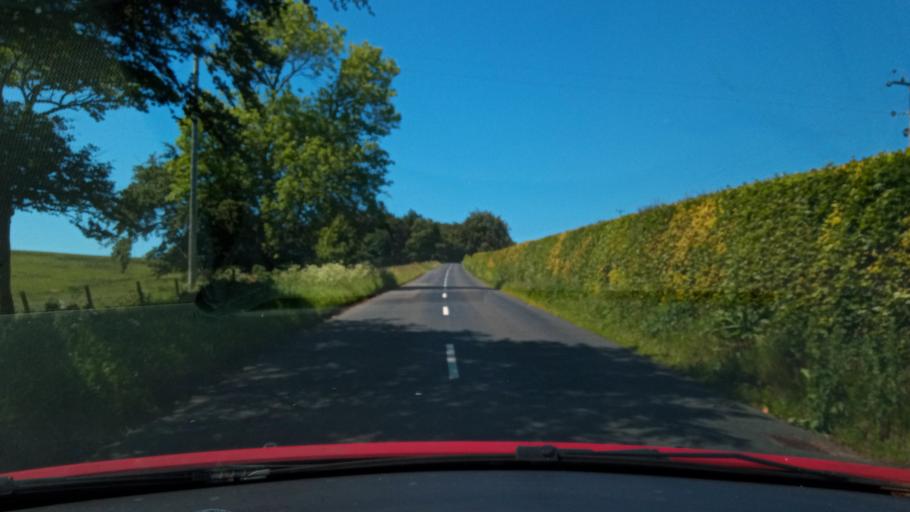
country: GB
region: Scotland
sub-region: The Scottish Borders
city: Duns
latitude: 55.7768
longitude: -2.4035
